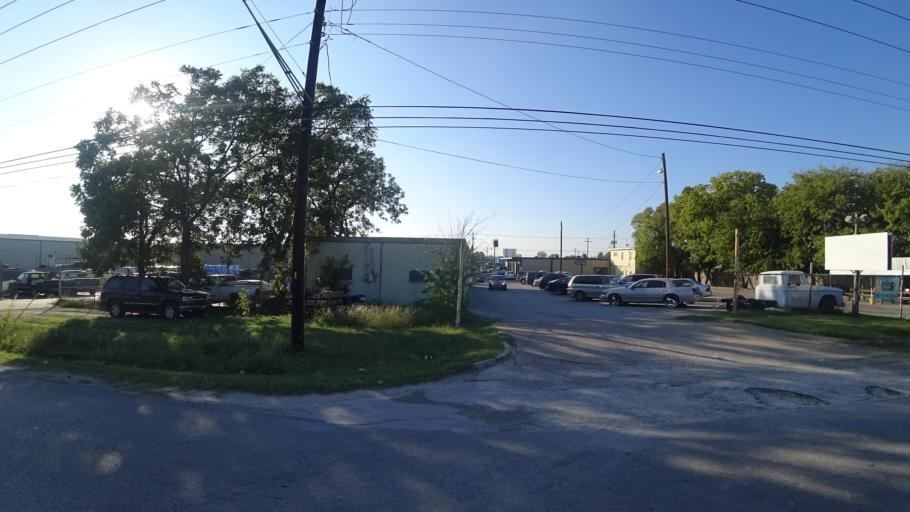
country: US
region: Texas
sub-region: Travis County
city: Wells Branch
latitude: 30.3596
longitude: -97.6851
